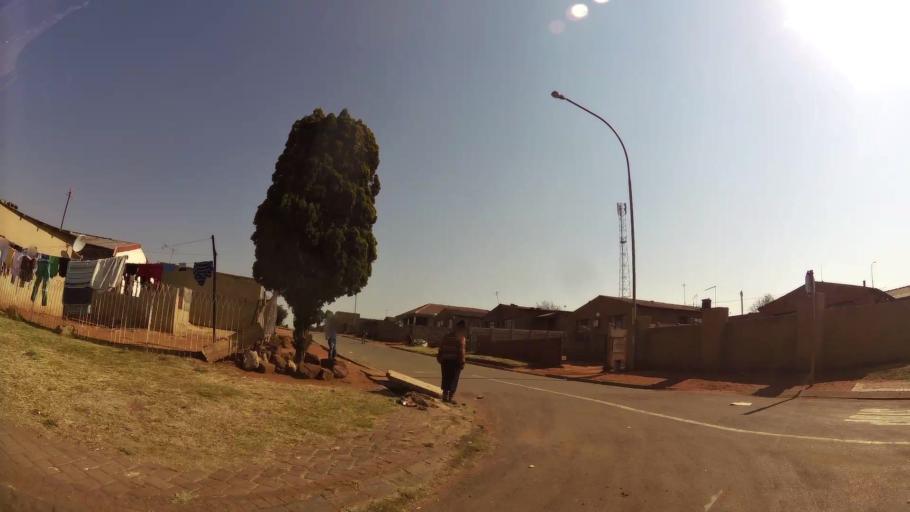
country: ZA
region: Gauteng
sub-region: Ekurhuleni Metropolitan Municipality
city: Benoni
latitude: -26.2285
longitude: 28.3081
